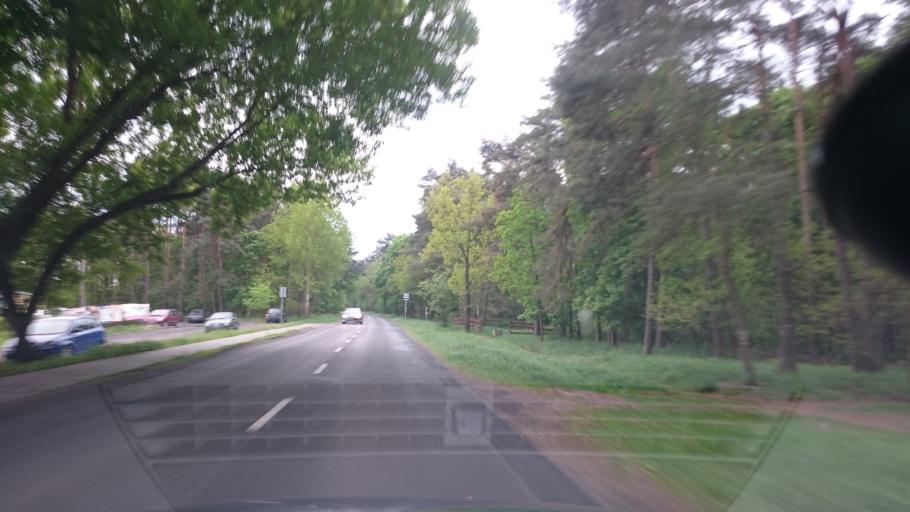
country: PL
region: Kujawsko-Pomorskie
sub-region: Grudziadz
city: Grudziadz
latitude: 53.4530
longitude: 18.7748
